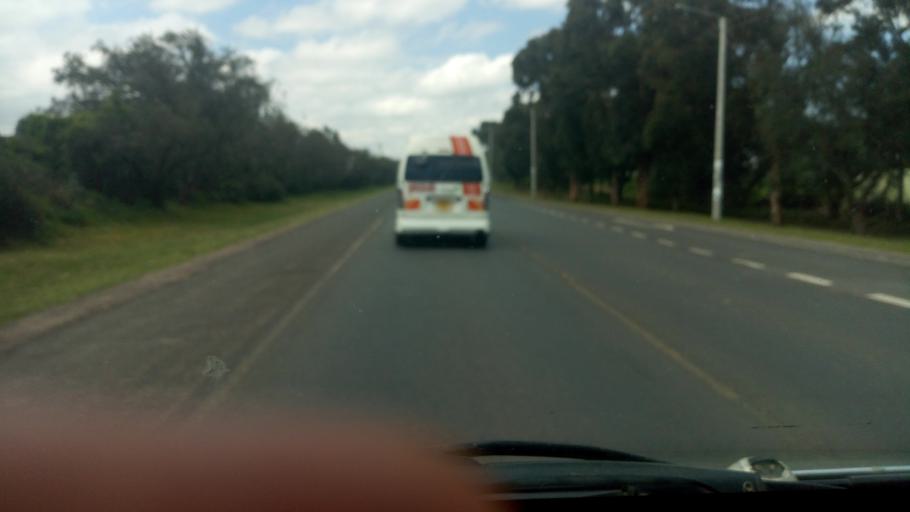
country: KE
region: Nakuru
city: Naivasha
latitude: -0.7000
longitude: 36.4315
